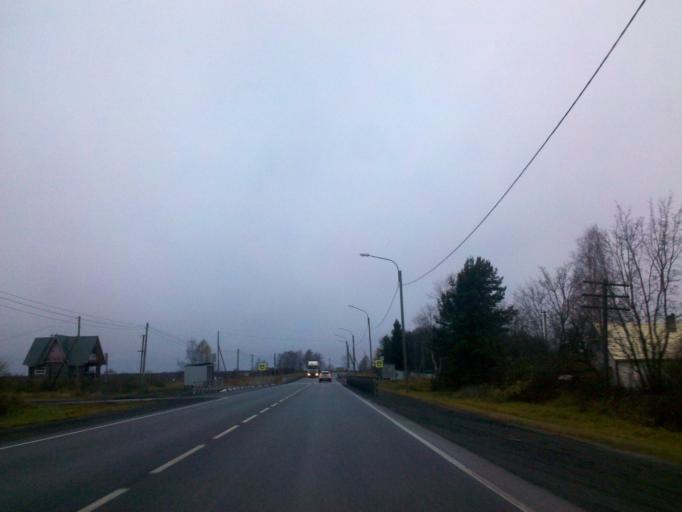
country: RU
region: Republic of Karelia
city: Shuya
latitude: 61.8158
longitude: 34.1018
